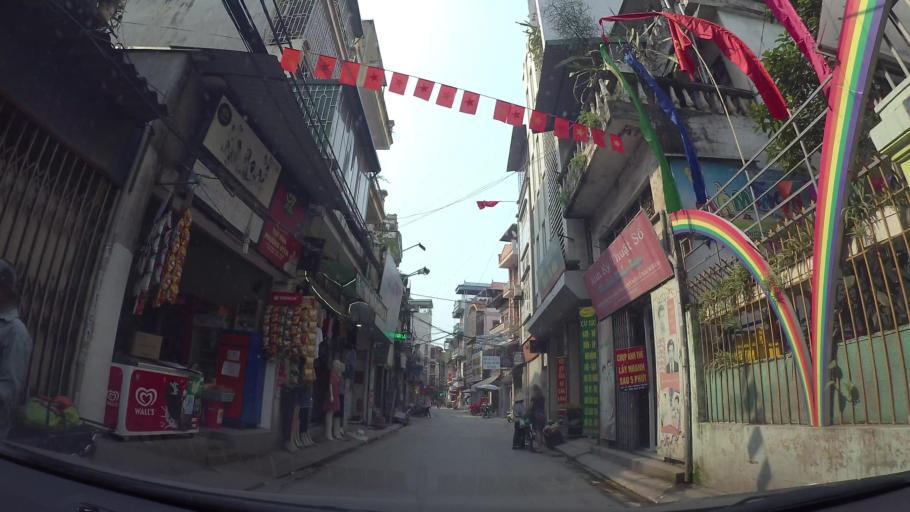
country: VN
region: Ha Noi
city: Thanh Xuan
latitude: 20.9906
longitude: 105.8175
